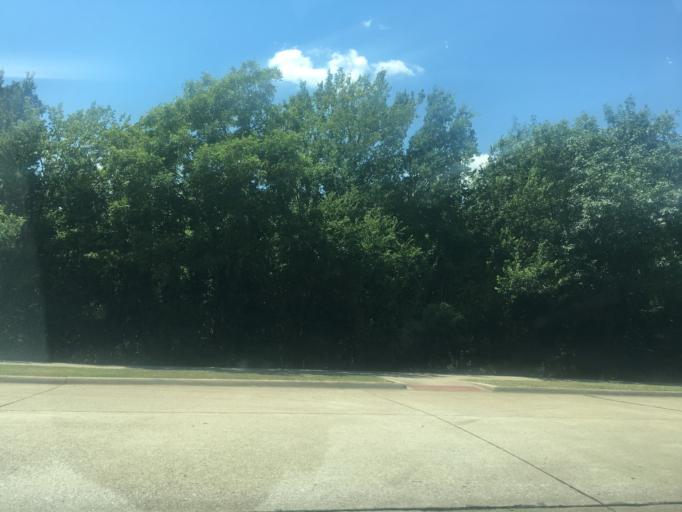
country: US
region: Texas
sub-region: Denton County
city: Lewisville
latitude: 33.0215
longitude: -97.0008
